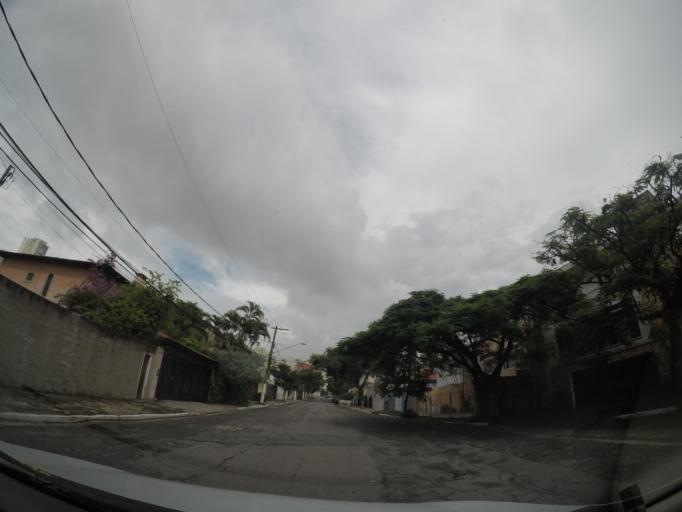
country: BR
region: Sao Paulo
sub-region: Sao Paulo
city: Sao Paulo
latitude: -23.5881
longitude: -46.6232
